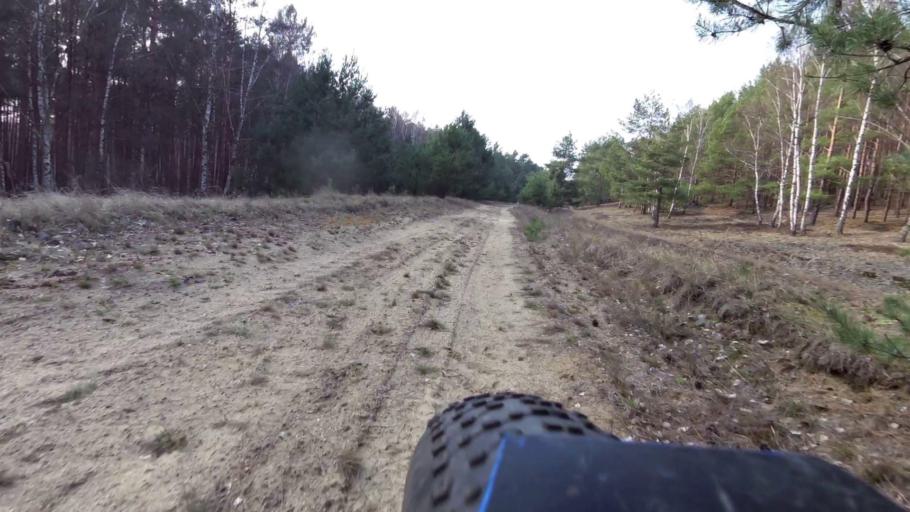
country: PL
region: Lubusz
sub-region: Powiat slubicki
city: Cybinka
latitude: 52.2471
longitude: 14.7528
